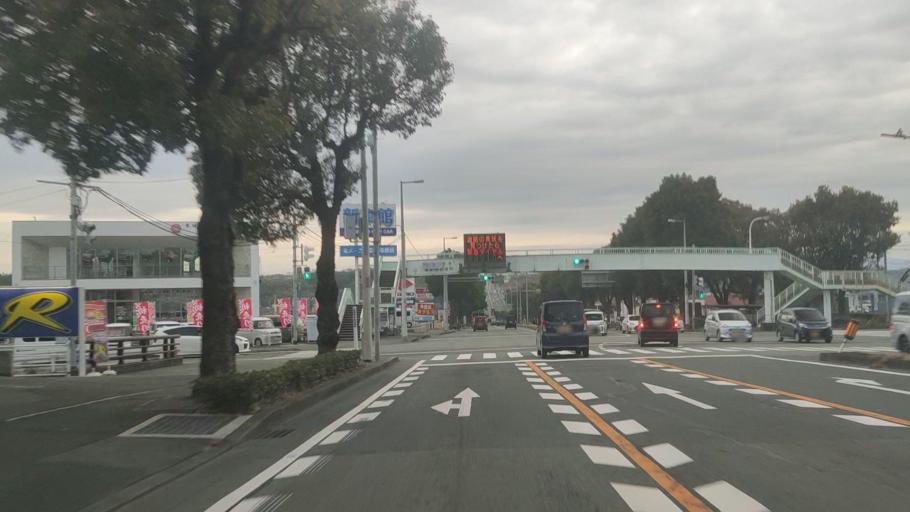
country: JP
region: Kumamoto
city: Ozu
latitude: 32.8425
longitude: 130.7806
